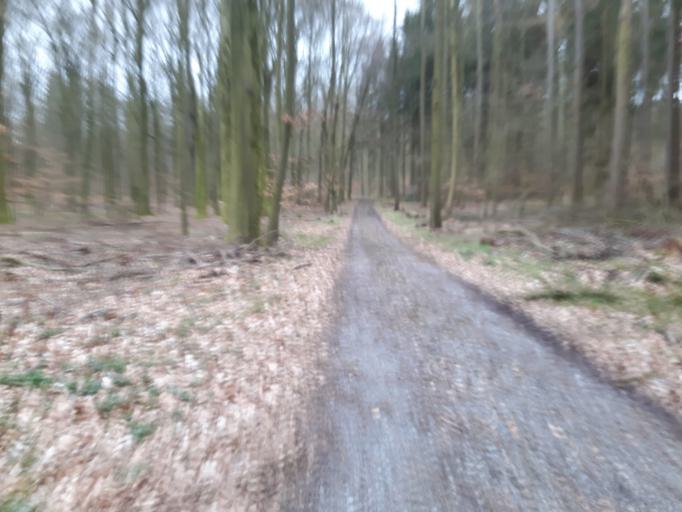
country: DE
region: Baden-Wuerttemberg
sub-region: Regierungsbezirk Stuttgart
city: Leingarten
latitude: 49.1770
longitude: 9.0869
